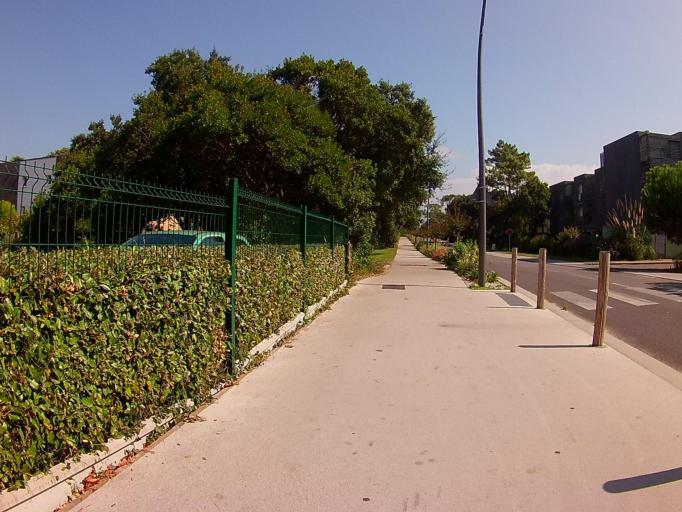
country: FR
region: Aquitaine
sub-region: Departement des Landes
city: Ondres
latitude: 43.5980
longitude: -1.4687
